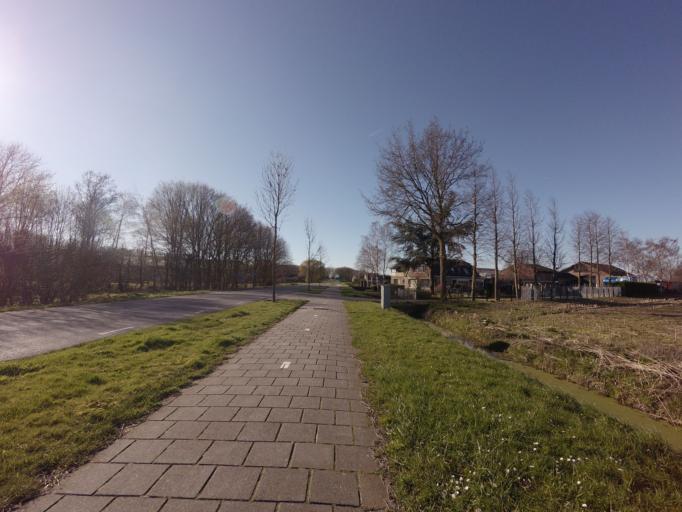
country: NL
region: Utrecht
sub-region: Gemeente Wijk bij Duurstede
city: Wijk bij Duurstede
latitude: 51.9546
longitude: 5.3644
